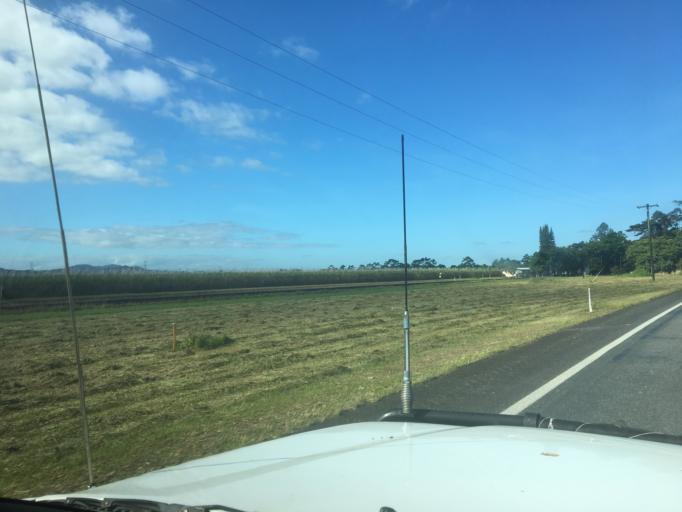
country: AU
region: Queensland
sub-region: Cassowary Coast
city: Innisfail
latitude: -17.3057
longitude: 145.9274
